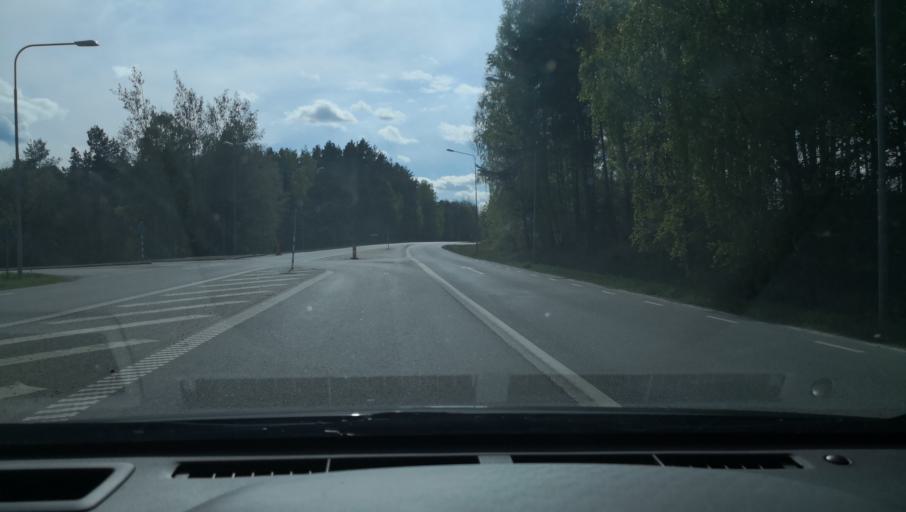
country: SE
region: OErebro
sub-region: Askersunds Kommun
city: Asbro
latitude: 59.0536
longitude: 15.0507
